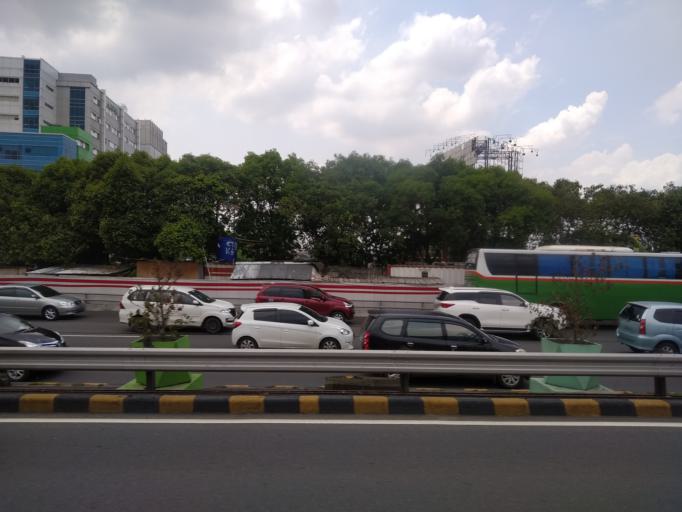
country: ID
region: Jakarta Raya
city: Jakarta
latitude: -6.2452
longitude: 106.8701
